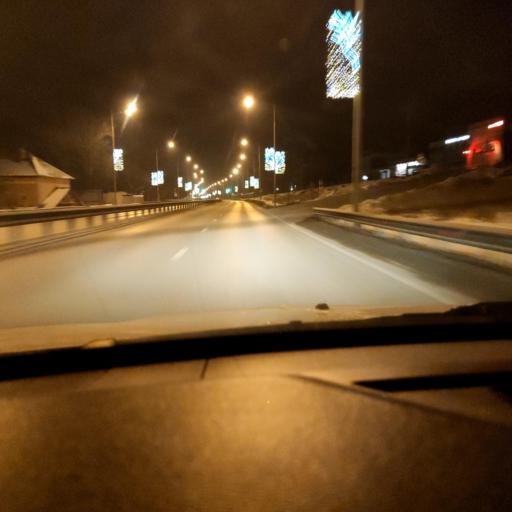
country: RU
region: Samara
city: Volzhskiy
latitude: 53.4005
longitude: 50.1483
